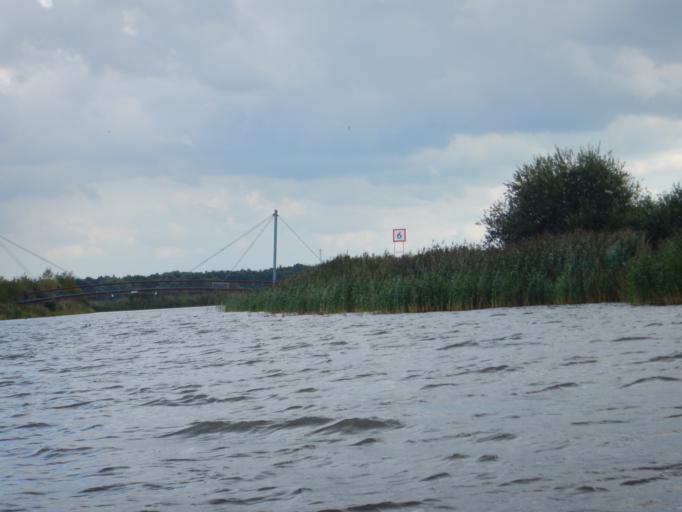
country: NL
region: Groningen
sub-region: Gemeente  Oldambt
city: Winschoten
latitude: 53.1848
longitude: 7.0550
